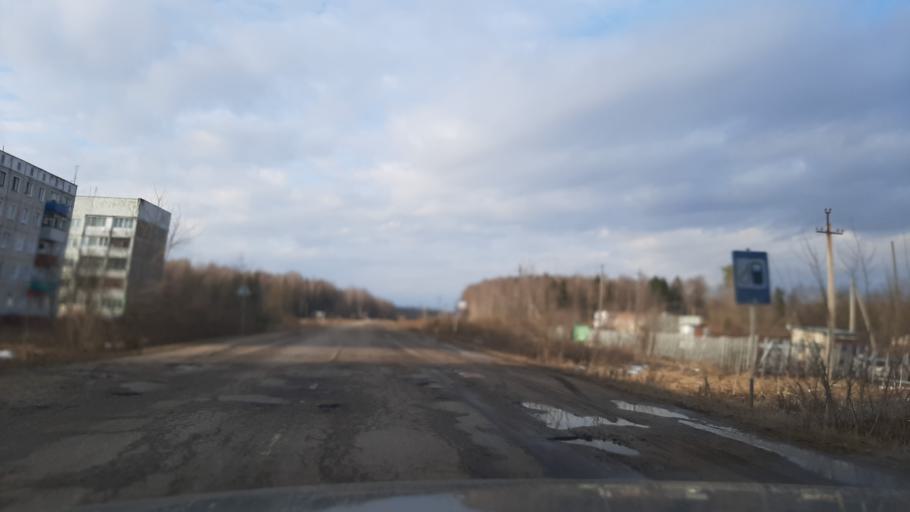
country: RU
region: Ivanovo
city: Novo-Talitsy
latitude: 56.9242
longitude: 40.7381
